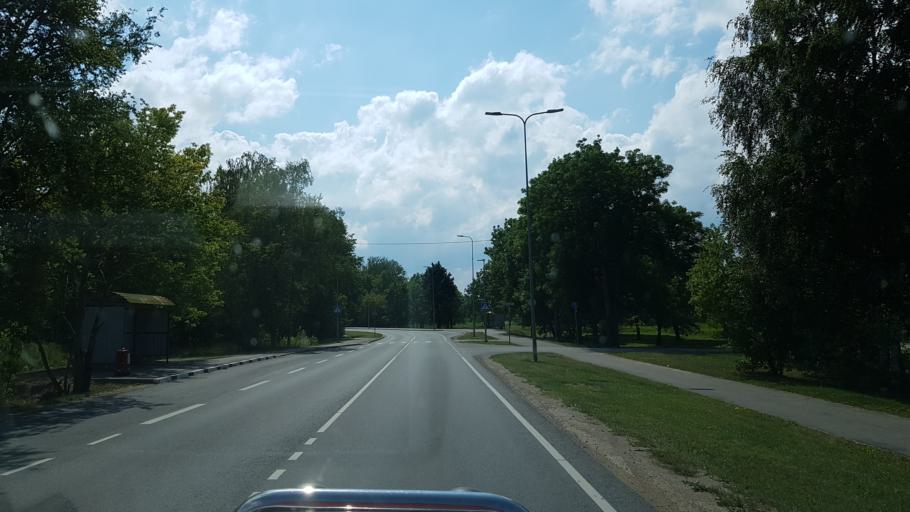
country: EE
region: Ida-Virumaa
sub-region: Kohtla-Jaerve linn
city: Kohtla-Jarve
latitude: 59.3789
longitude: 27.2559
